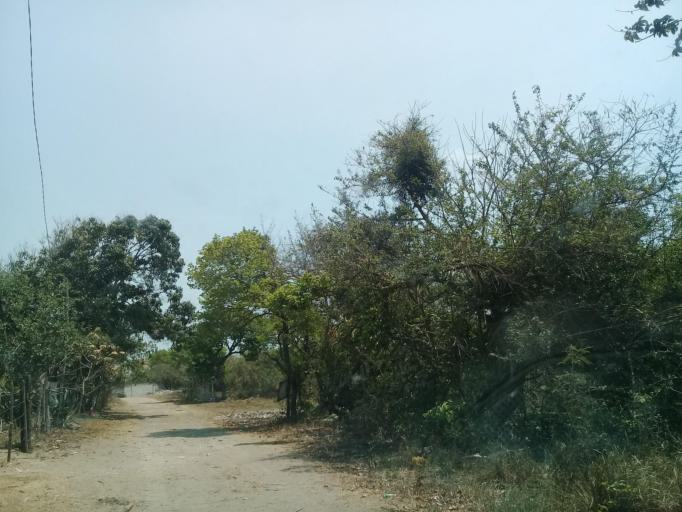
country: MX
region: Veracruz
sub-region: Veracruz
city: Hacienda Sotavento
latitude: 19.1340
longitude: -96.1830
